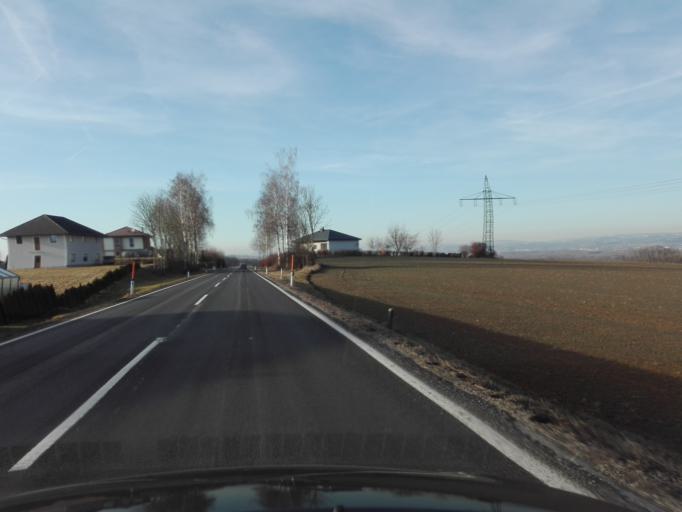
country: AT
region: Lower Austria
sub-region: Politischer Bezirk Amstetten
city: Strengberg
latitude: 48.1614
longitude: 14.6158
